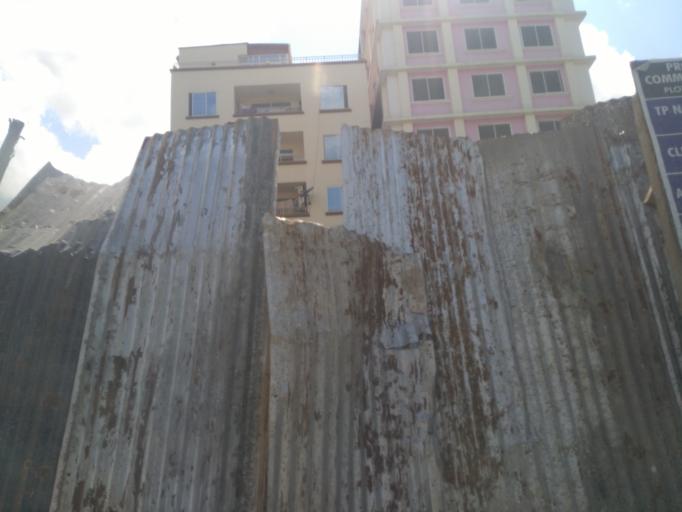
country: TZ
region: Dar es Salaam
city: Dar es Salaam
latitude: -6.8180
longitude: 39.2719
